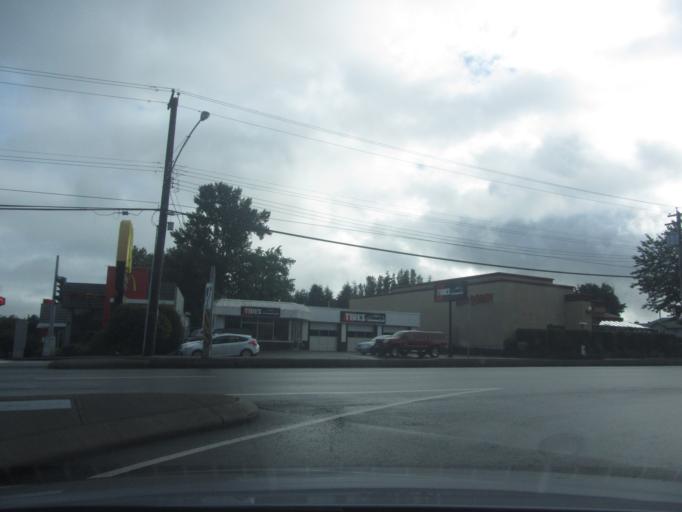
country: CA
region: British Columbia
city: Abbotsford
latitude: 49.0507
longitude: -122.3098
